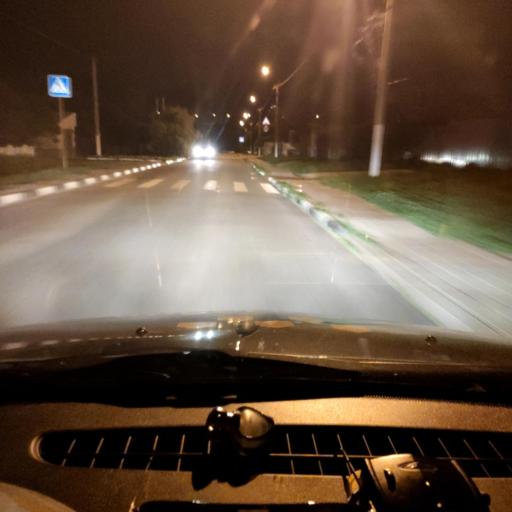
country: RU
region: Belgorod
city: Mayskiy
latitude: 50.5181
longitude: 36.4603
